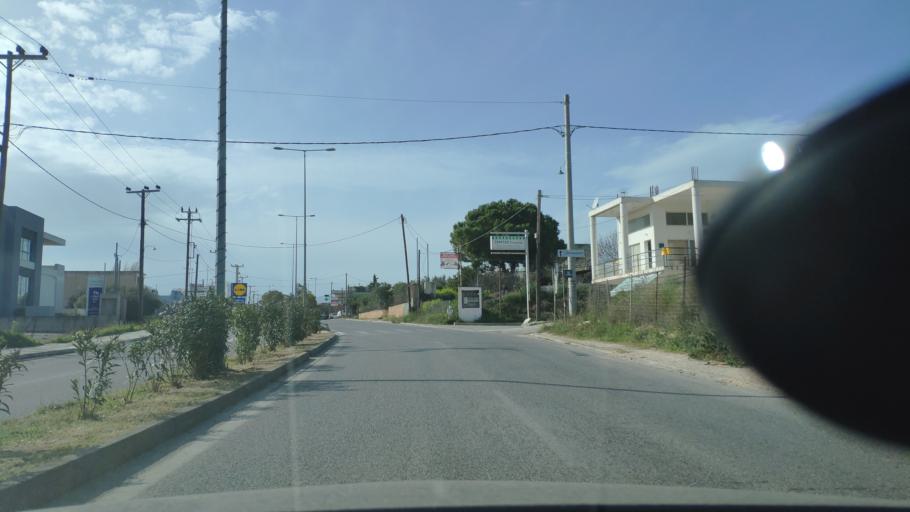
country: GR
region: Attica
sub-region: Nomarchia Anatolikis Attikis
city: Limin Mesoyaias
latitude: 37.8934
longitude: 23.9910
